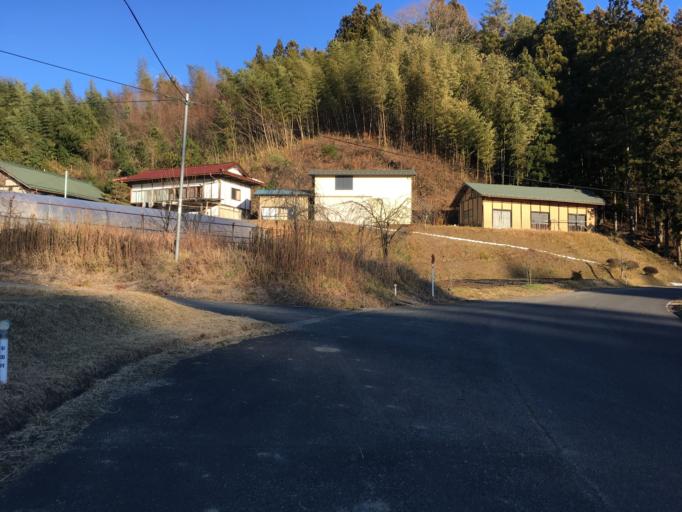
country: JP
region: Fukushima
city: Ishikawa
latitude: 37.1681
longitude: 140.5466
